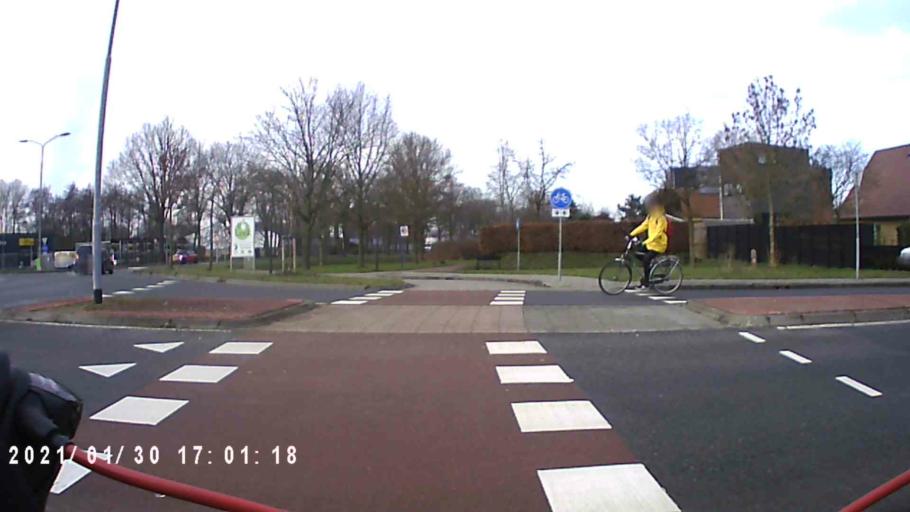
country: NL
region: Groningen
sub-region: Gemeente Leek
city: Leek
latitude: 53.1509
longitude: 6.3720
